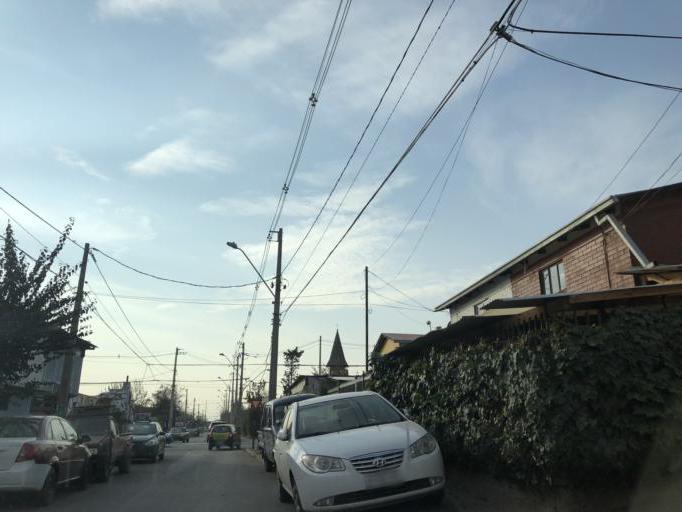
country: CL
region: Santiago Metropolitan
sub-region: Provincia de Cordillera
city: Puente Alto
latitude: -33.6044
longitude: -70.5598
